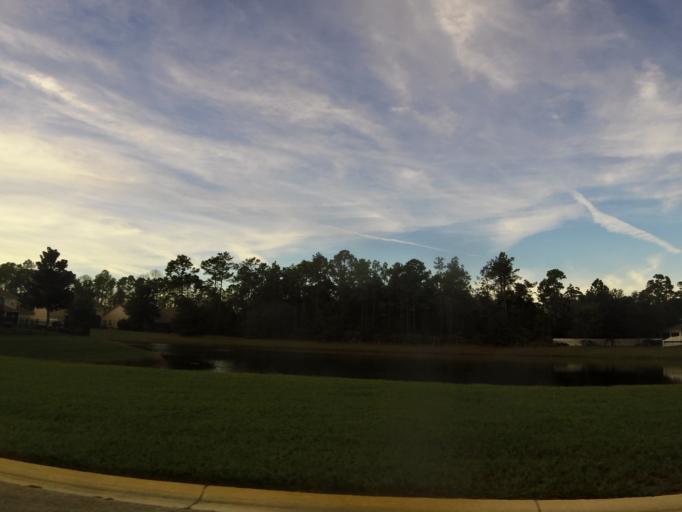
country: US
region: Florida
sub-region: Saint Johns County
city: Fruit Cove
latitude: 30.1507
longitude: -81.5339
